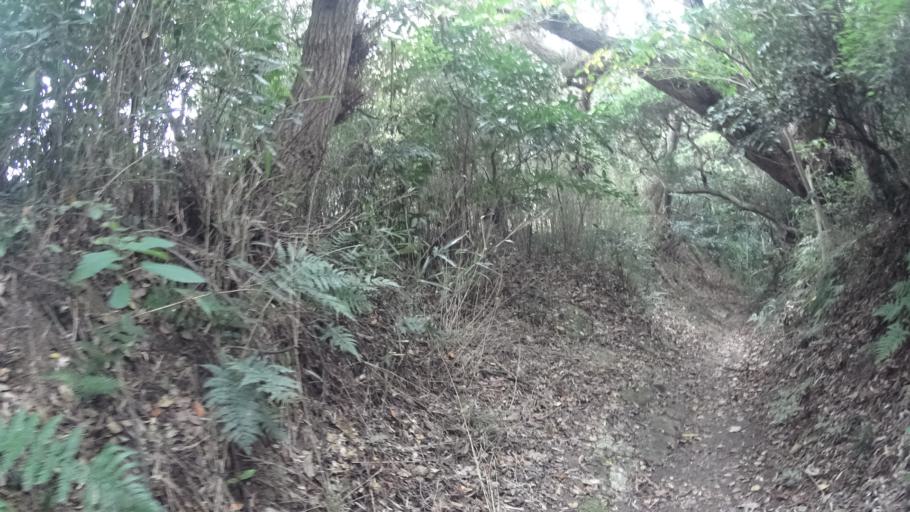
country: JP
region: Kanagawa
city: Zushi
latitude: 35.2911
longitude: 139.6059
